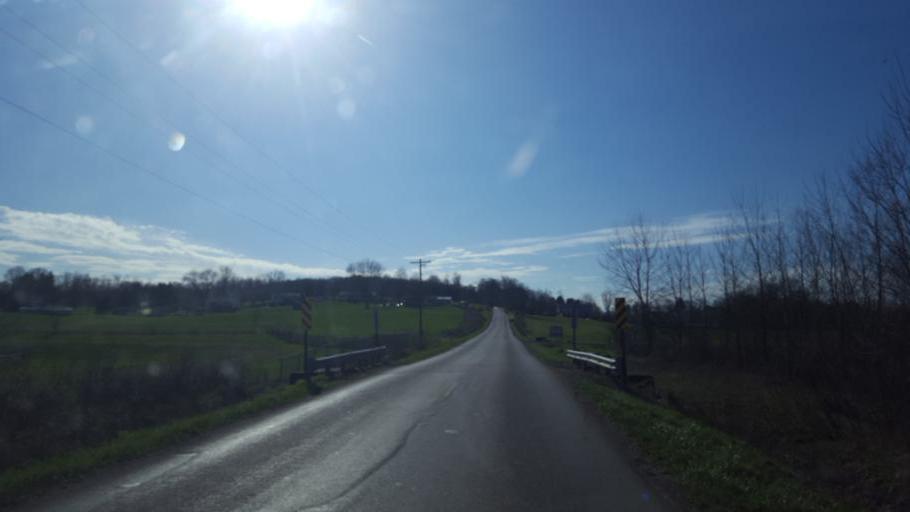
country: US
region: Ohio
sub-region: Knox County
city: Danville
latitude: 40.4514
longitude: -82.2654
